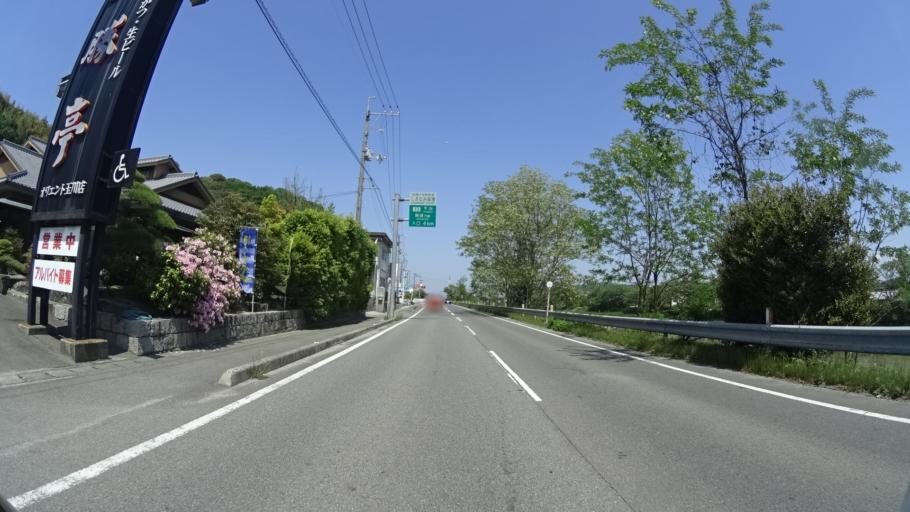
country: JP
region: Ehime
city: Hojo
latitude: 34.0284
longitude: 132.9621
